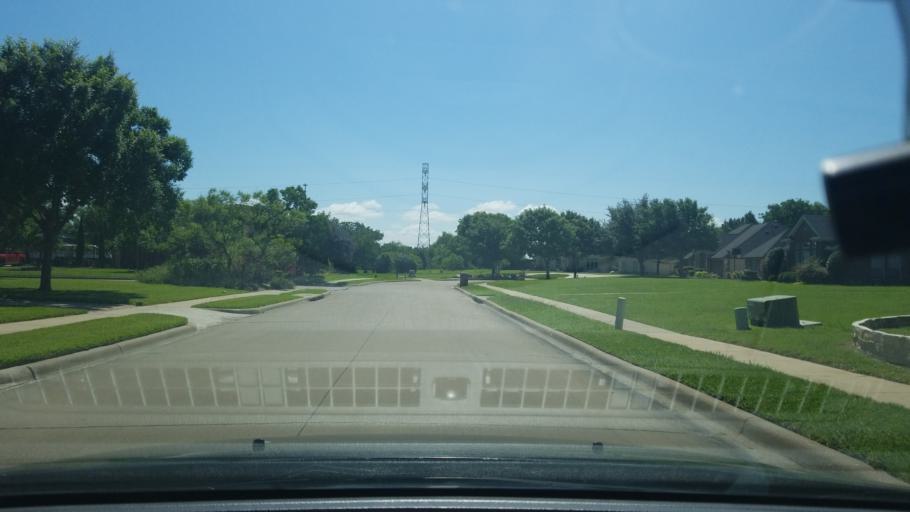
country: US
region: Texas
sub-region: Dallas County
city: Sunnyvale
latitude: 32.7897
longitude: -96.5751
